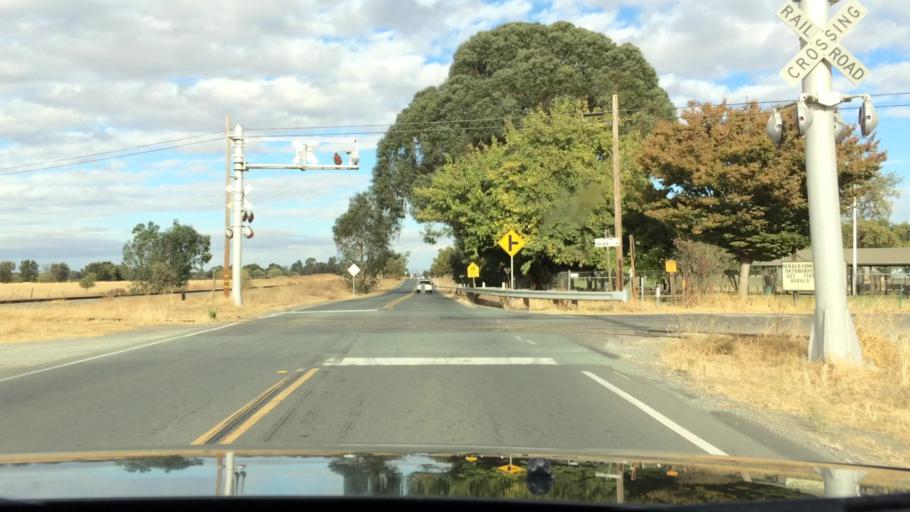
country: US
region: California
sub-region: Sacramento County
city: Herald
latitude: 38.2954
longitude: -121.2449
